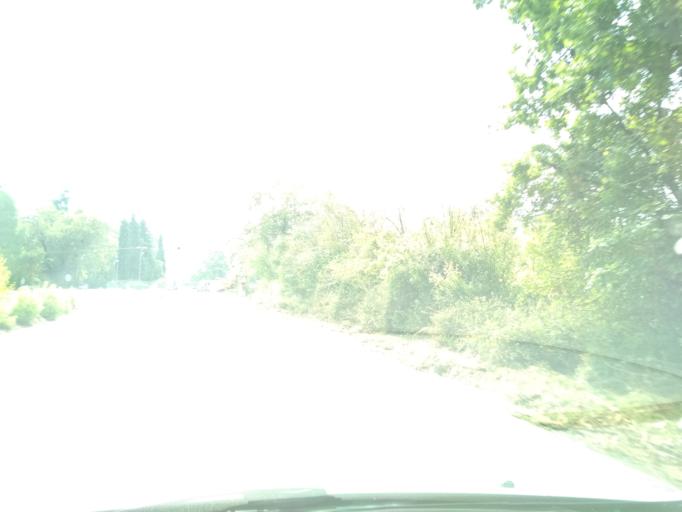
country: GR
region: Central Greece
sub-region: Nomos Evvoias
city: Prokopion
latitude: 38.7251
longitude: 23.5052
